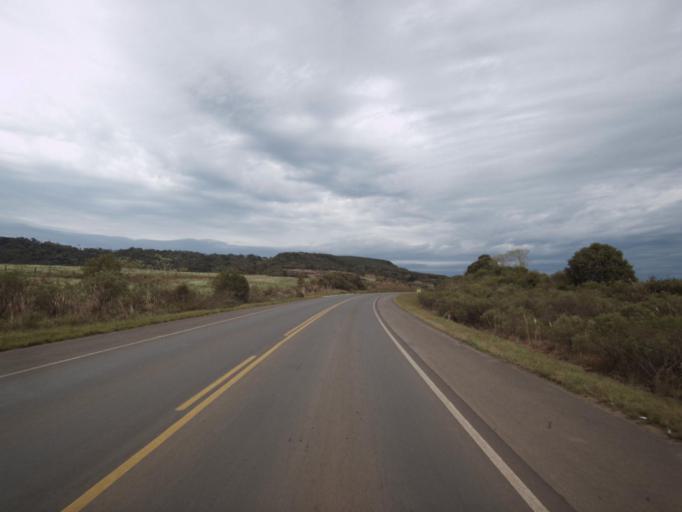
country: BR
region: Santa Catarina
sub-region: Concordia
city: Concordia
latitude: -26.9463
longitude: -51.8245
